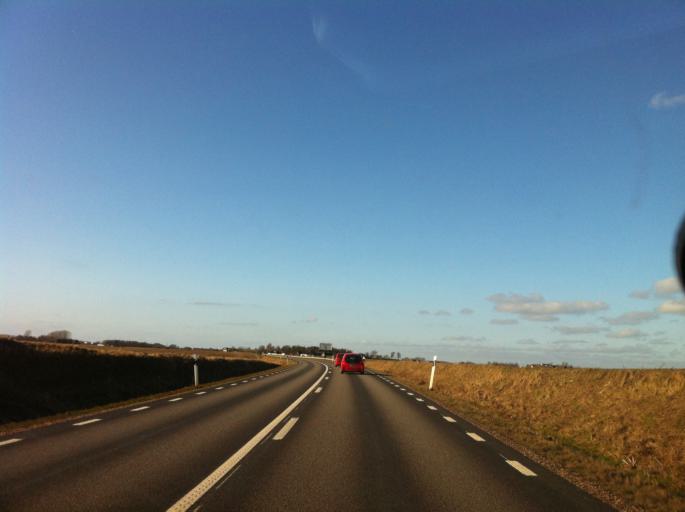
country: SE
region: Skane
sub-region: Svedala Kommun
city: Klagerup
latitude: 55.5483
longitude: 13.2685
